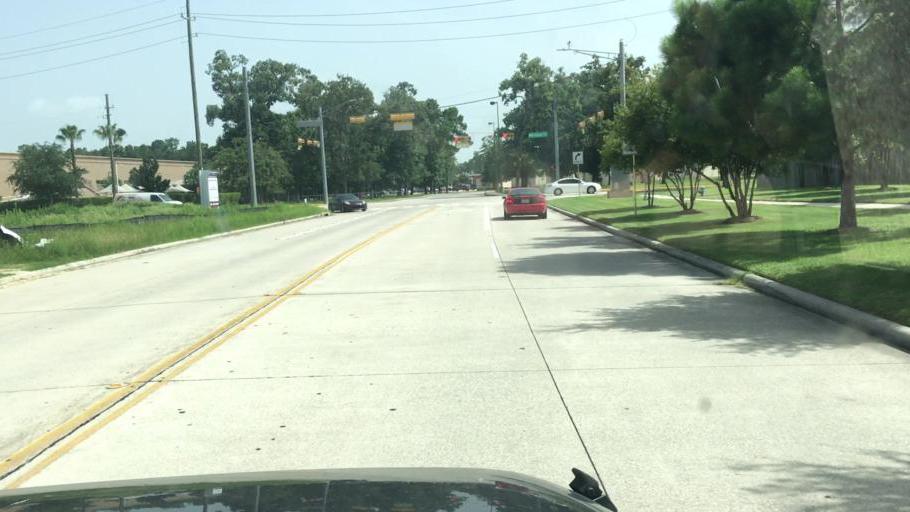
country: US
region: Texas
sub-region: Harris County
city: Atascocita
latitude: 29.9827
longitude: -95.1695
